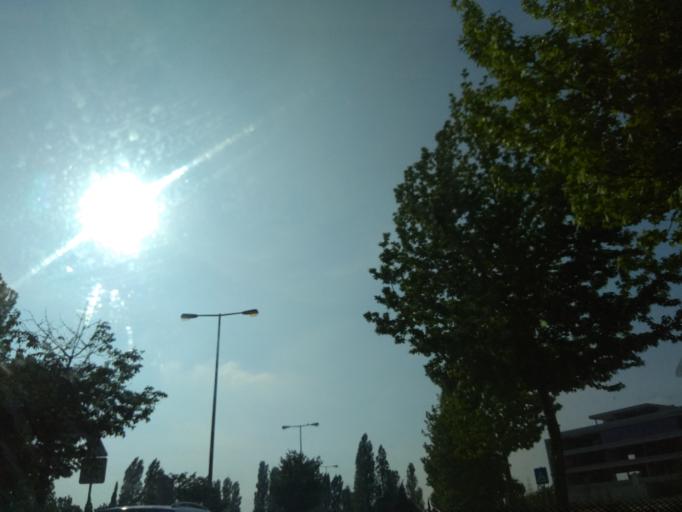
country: PT
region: Porto
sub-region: Maia
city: Maia
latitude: 41.2267
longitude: -8.6247
